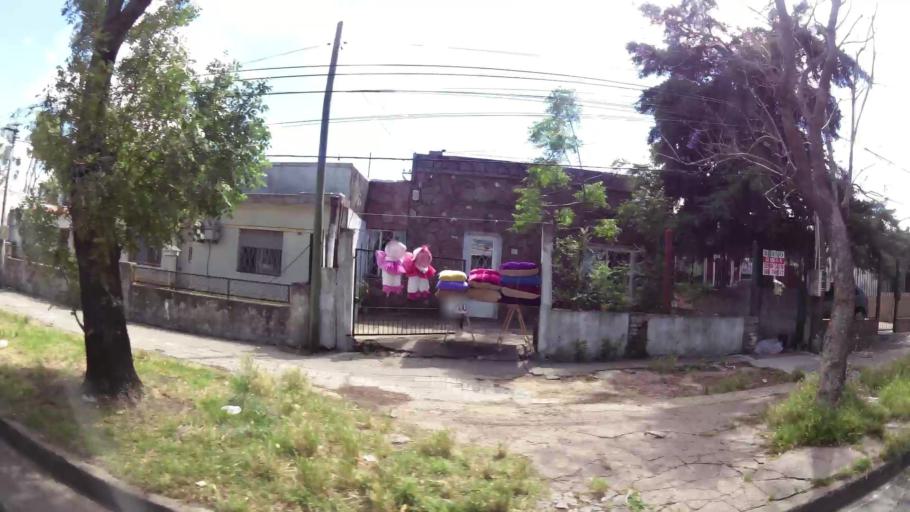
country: UY
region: Montevideo
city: Montevideo
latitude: -34.8526
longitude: -56.1456
